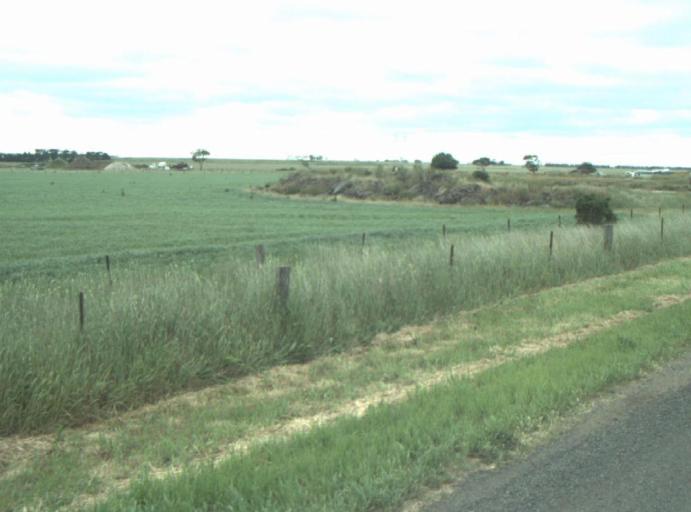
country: AU
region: Victoria
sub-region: Greater Geelong
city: Bell Post Hill
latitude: -38.0269
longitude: 144.2905
